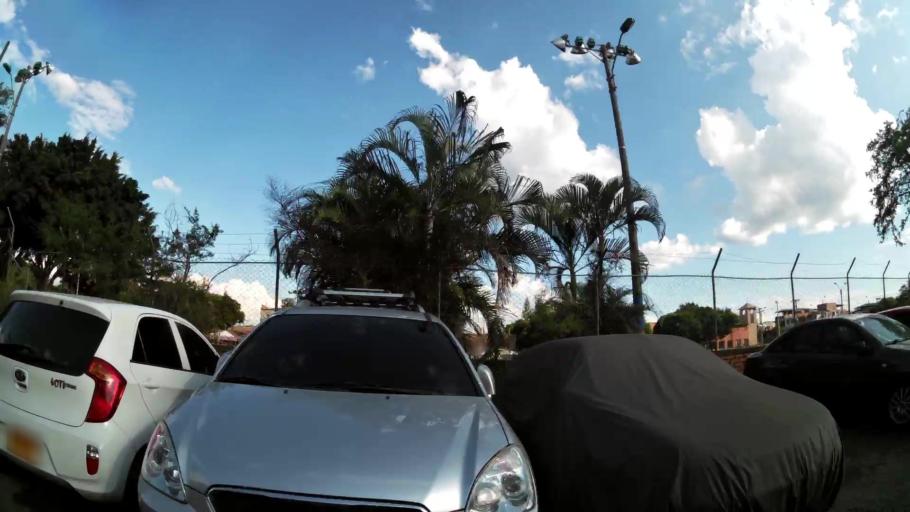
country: CO
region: Valle del Cauca
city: Cali
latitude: 3.4012
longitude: -76.5089
